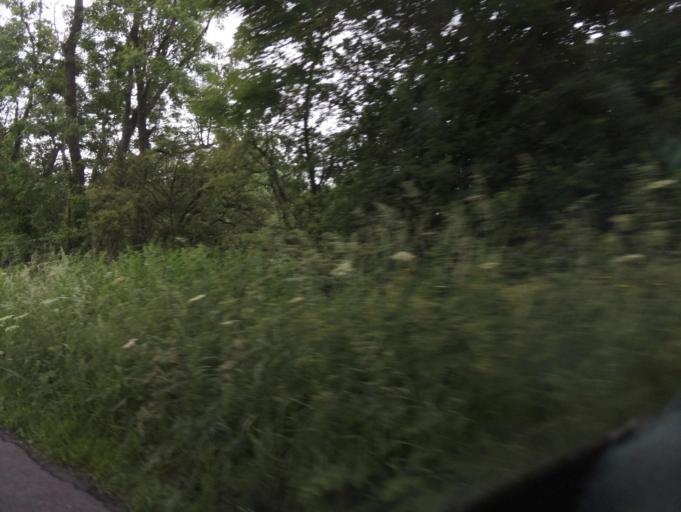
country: GB
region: England
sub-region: District of Rutland
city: Langham
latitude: 52.6825
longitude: -0.8260
